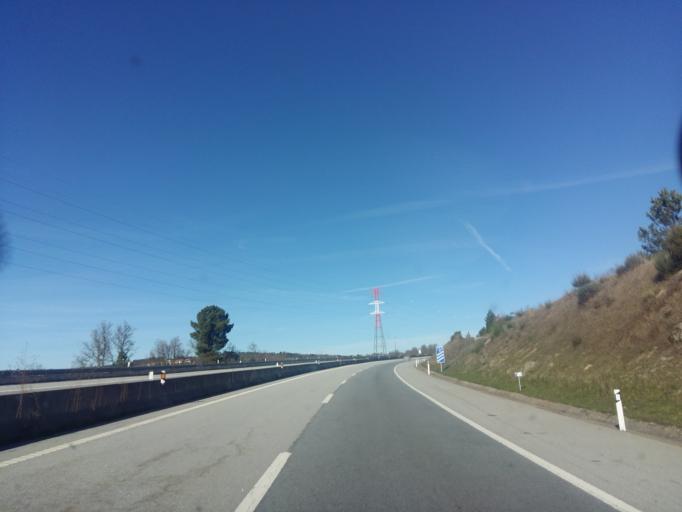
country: PT
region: Guarda
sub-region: Guarda
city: Sequeira
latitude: 40.5511
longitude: -7.2173
